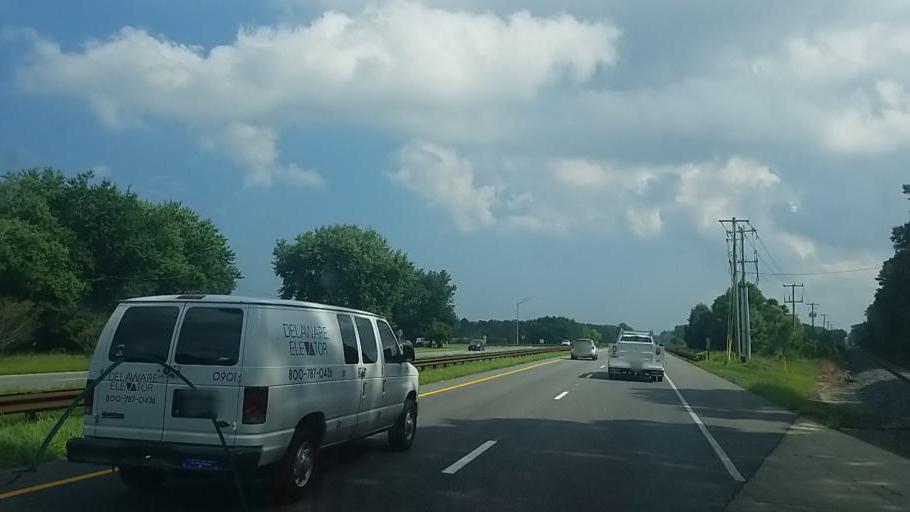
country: US
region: Delaware
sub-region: Sussex County
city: Selbyville
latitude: 38.4348
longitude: -75.2231
